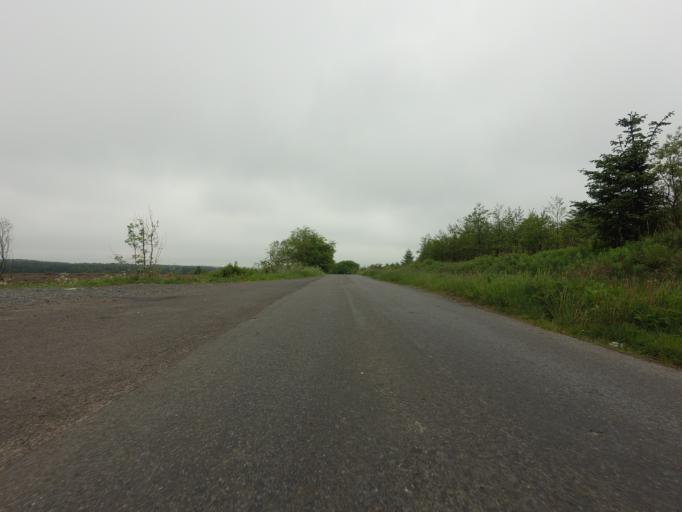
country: GB
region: Scotland
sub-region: Fife
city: Townhill
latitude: 56.1269
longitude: -3.4374
